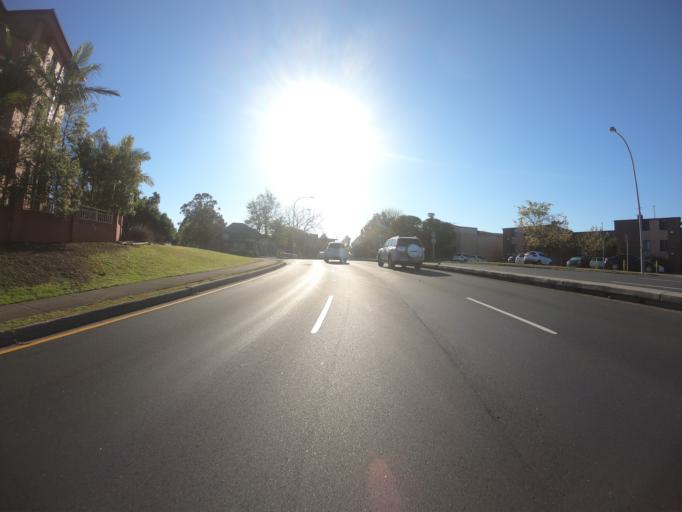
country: AU
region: New South Wales
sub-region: Canada Bay
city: Rhodes
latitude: -33.8168
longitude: 151.1055
